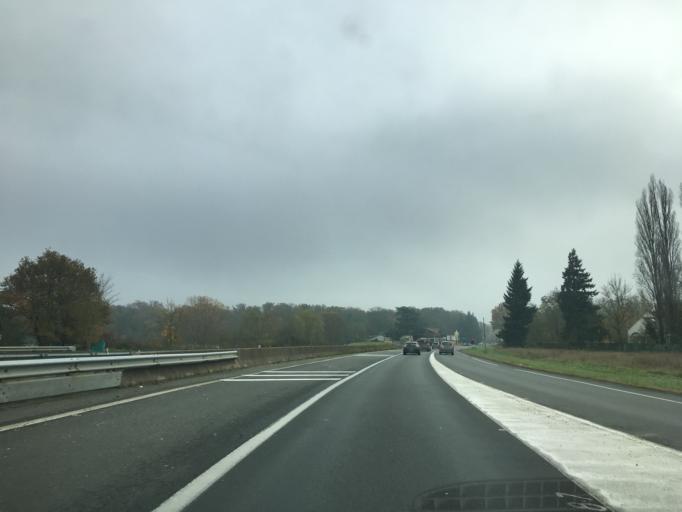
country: FR
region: Ile-de-France
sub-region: Departement de Seine-et-Marne
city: Chailly-en-Biere
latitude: 48.4546
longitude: 2.6184
